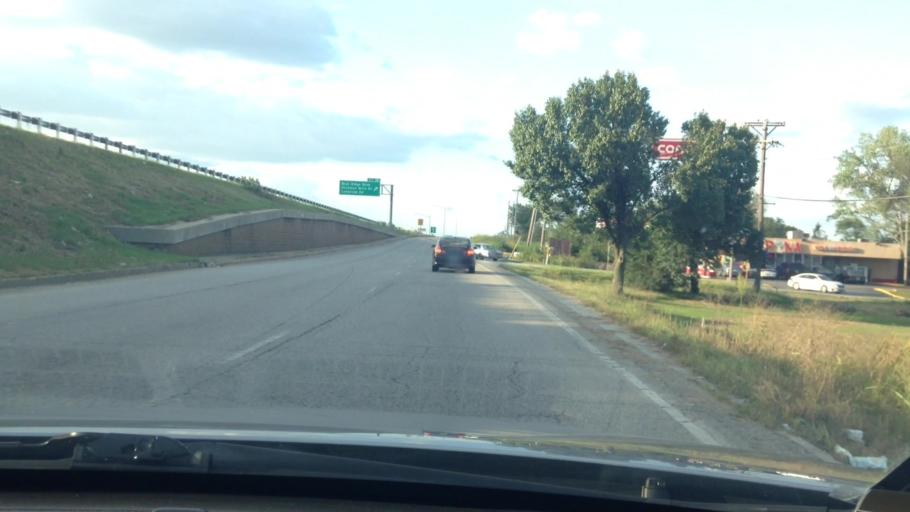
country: US
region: Missouri
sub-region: Jackson County
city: Grandview
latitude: 38.8972
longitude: -94.5241
